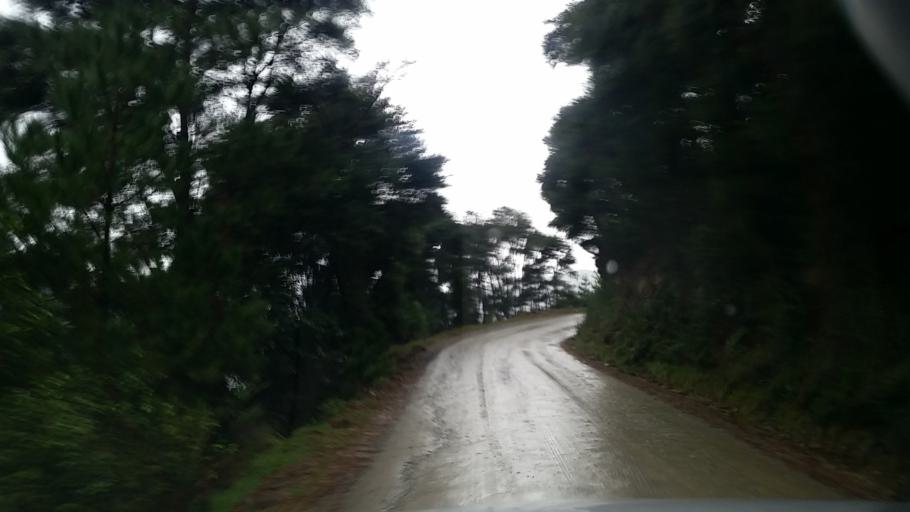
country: NZ
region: Marlborough
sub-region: Marlborough District
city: Picton
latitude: -41.1767
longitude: 174.0563
